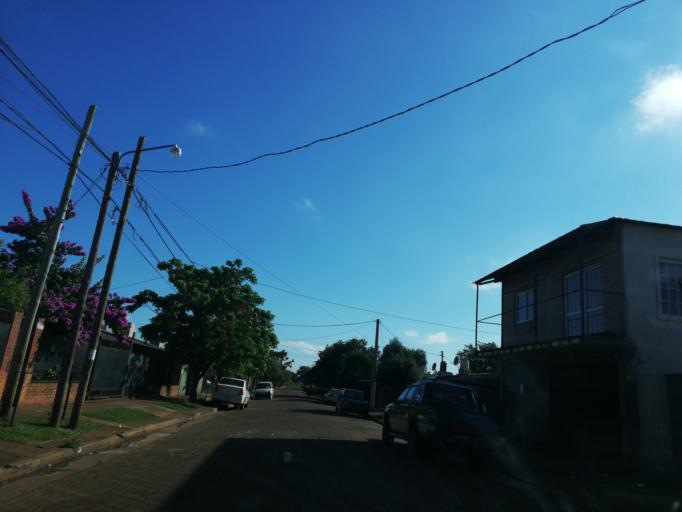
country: AR
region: Misiones
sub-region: Departamento de Capital
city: Posadas
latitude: -27.4261
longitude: -55.9395
